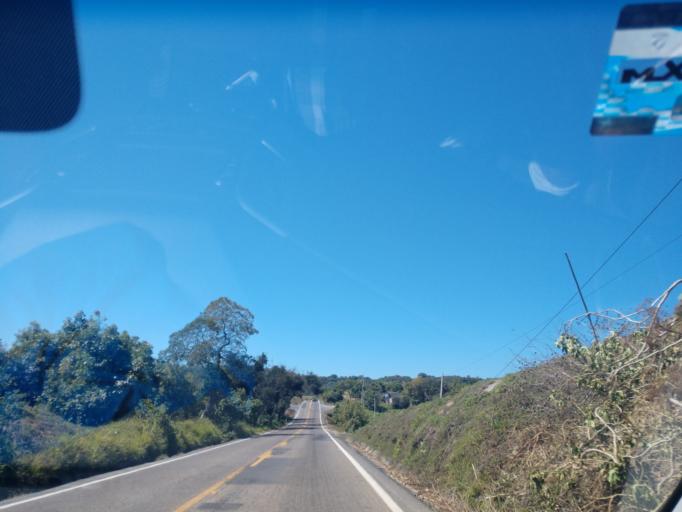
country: MX
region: Nayarit
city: Xalisco
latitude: 21.3698
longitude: -104.9111
